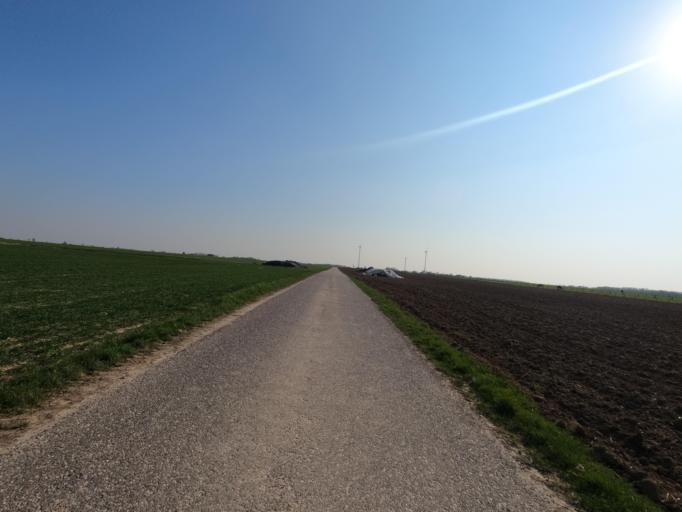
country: DE
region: North Rhine-Westphalia
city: Huckelhoven
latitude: 51.0814
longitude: 6.2552
